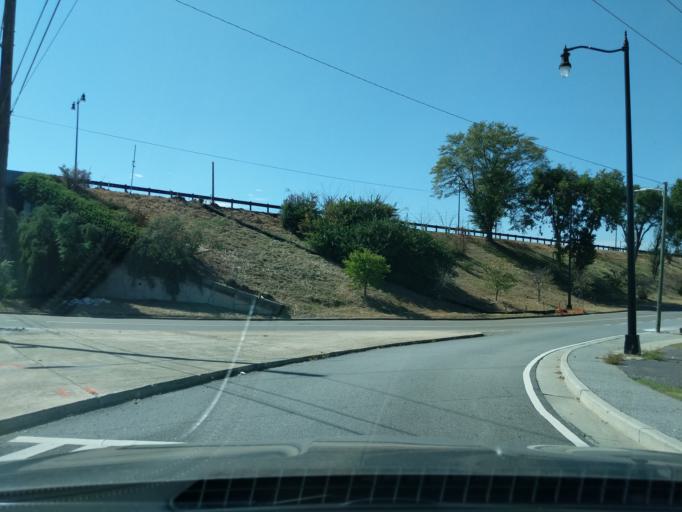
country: US
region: Georgia
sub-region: Richmond County
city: Augusta
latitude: 33.4782
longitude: -81.9847
